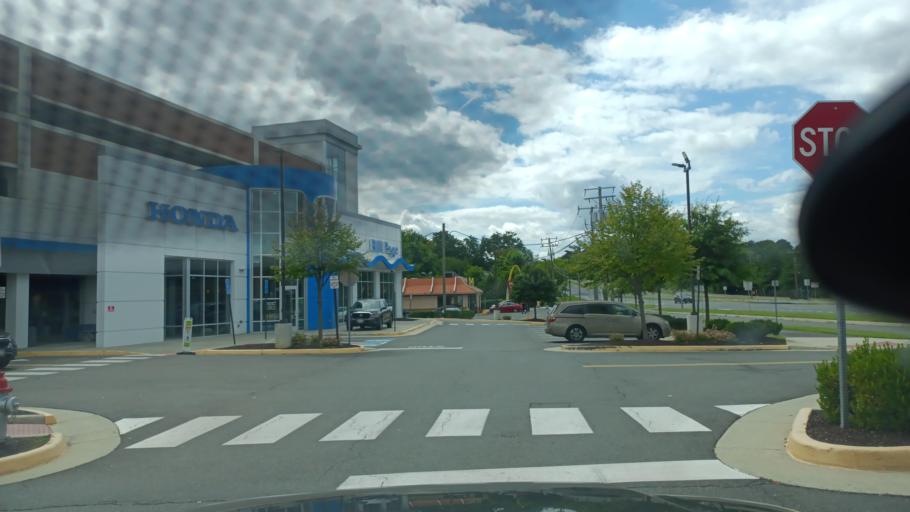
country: US
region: Virginia
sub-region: Fairfax County
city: Jefferson
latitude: 38.8691
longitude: -77.1756
